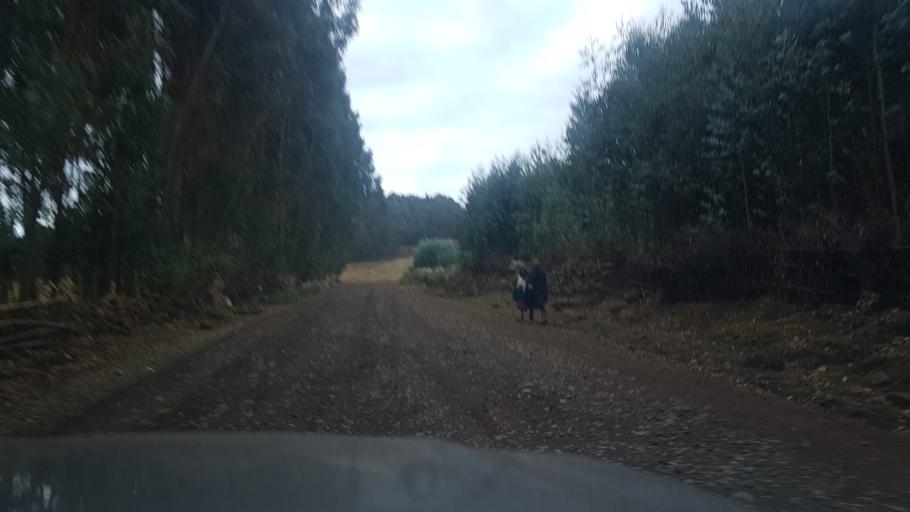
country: ET
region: Amhara
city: Finote Selam
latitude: 10.7994
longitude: 37.6636
